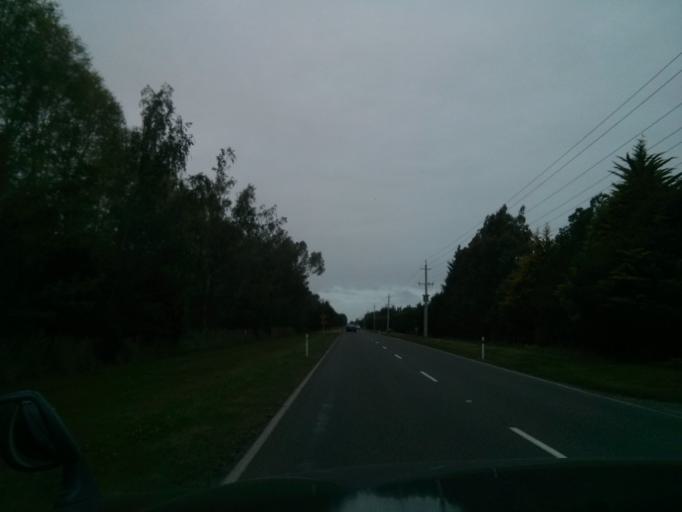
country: NZ
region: Canterbury
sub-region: Waimakariri District
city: Kaiapoi
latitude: -43.3764
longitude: 172.5239
